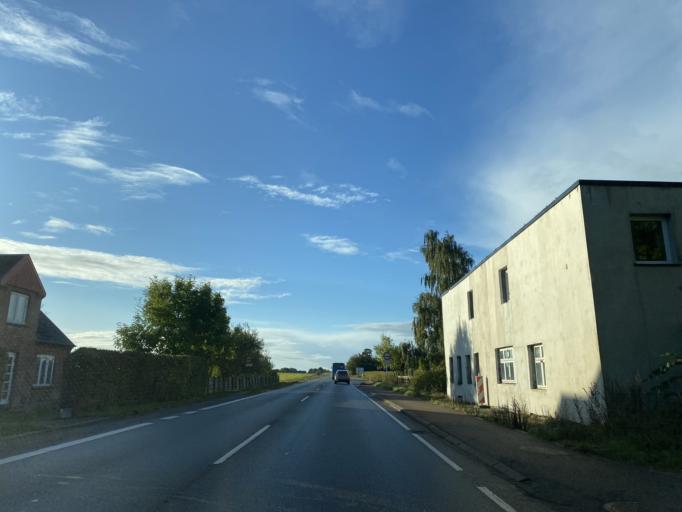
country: DK
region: Central Jutland
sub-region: Horsens Kommune
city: Braedstrup
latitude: 56.0026
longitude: 9.6045
